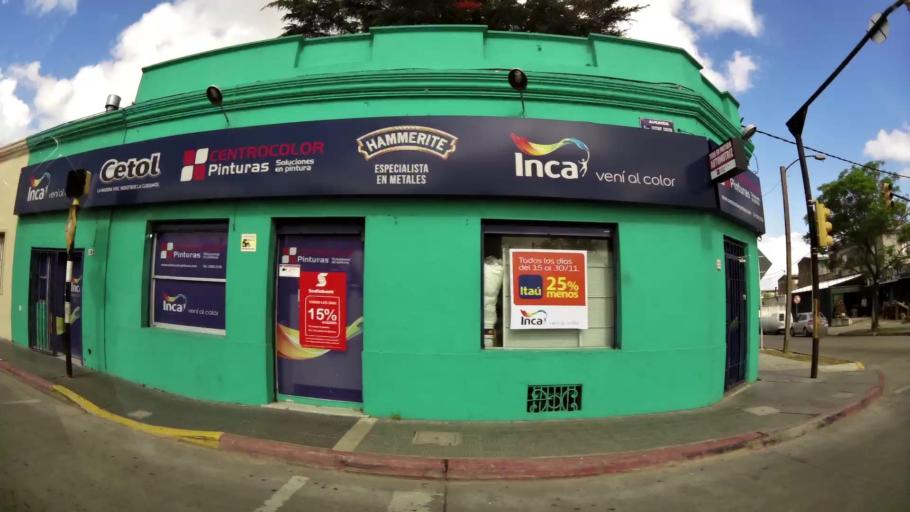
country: UY
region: Montevideo
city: Montevideo
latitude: -34.8490
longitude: -56.2233
